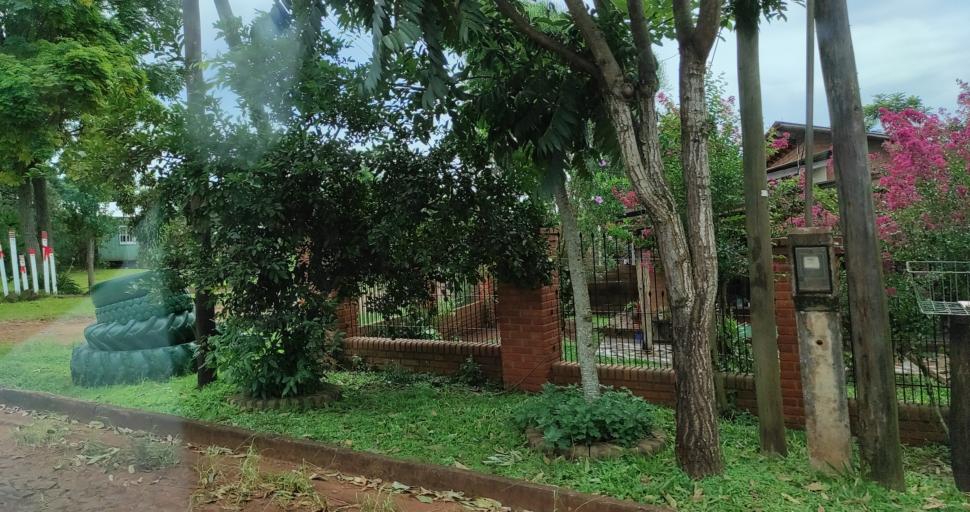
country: AR
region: Misiones
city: El Alcazar
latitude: -26.7188
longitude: -54.8137
